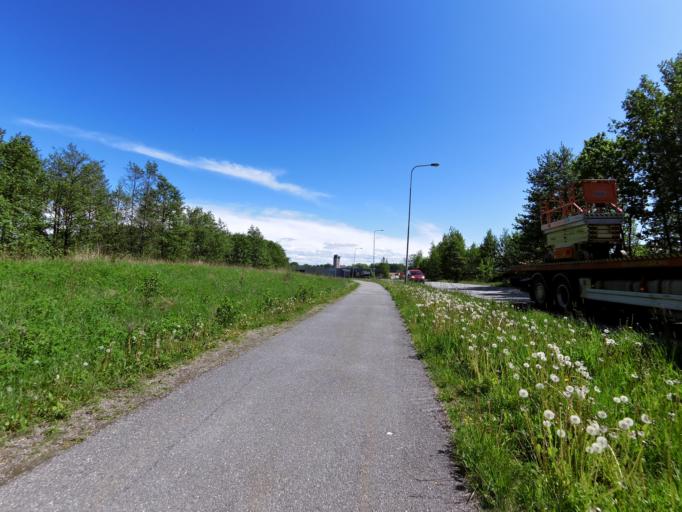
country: NO
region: Ostfold
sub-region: Fredrikstad
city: Fredrikstad
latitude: 59.2400
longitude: 10.9870
